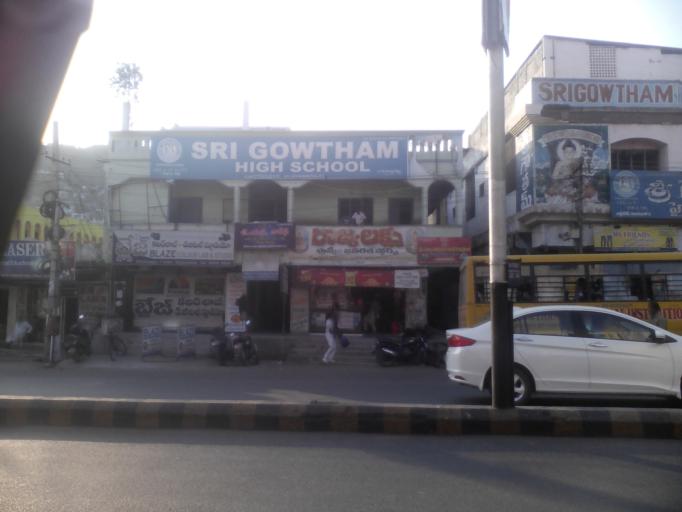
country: IN
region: Andhra Pradesh
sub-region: Krishna
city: Vijayawada
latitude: 16.5303
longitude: 80.6122
